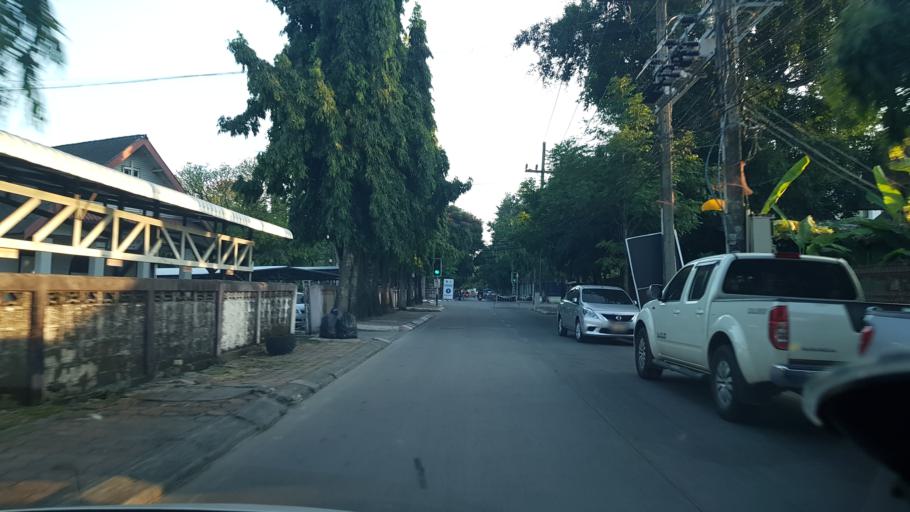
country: TH
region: Chiang Rai
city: Chiang Rai
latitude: 19.9119
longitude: 99.8347
